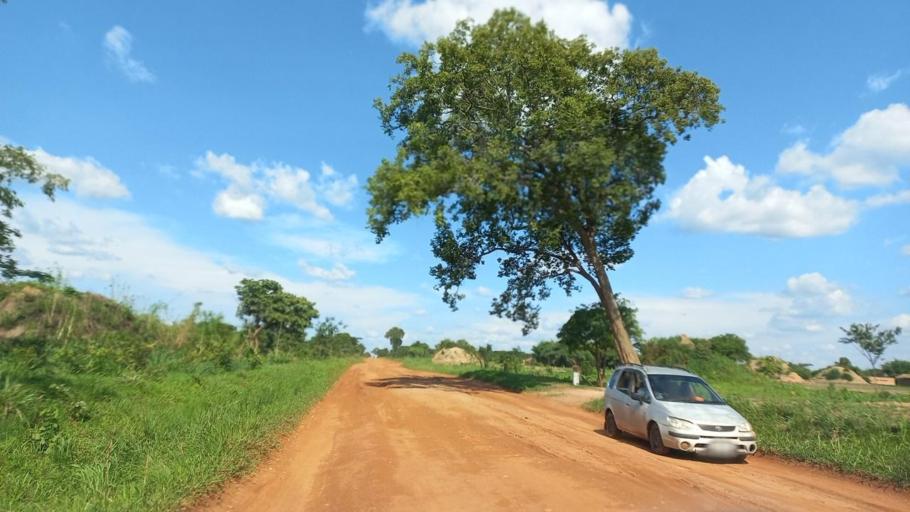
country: ZM
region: Copperbelt
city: Kitwe
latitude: -12.8692
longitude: 28.3623
